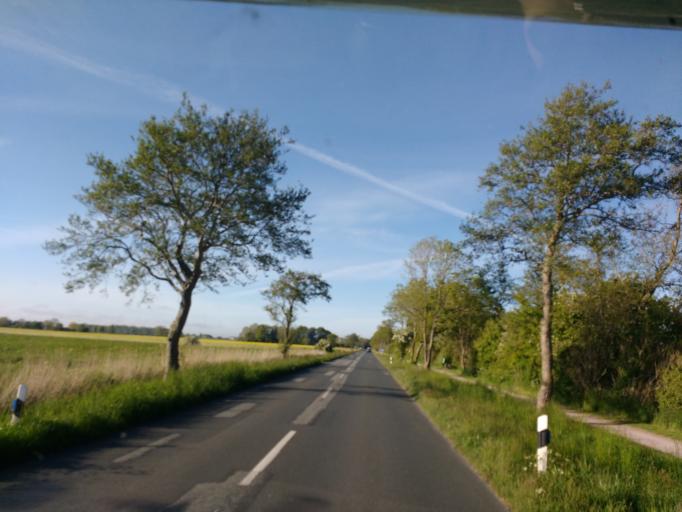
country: DE
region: Lower Saxony
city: Schillig
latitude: 53.6898
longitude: 8.0094
